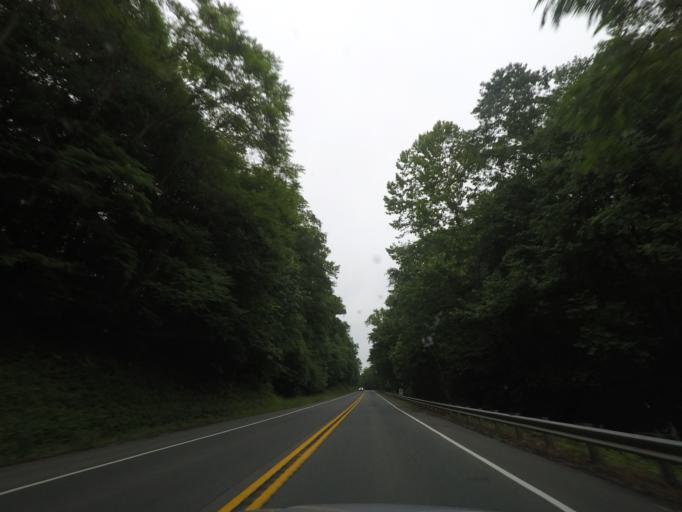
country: US
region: Virginia
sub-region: Fluvanna County
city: Weber City
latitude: 37.7192
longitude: -78.3007
